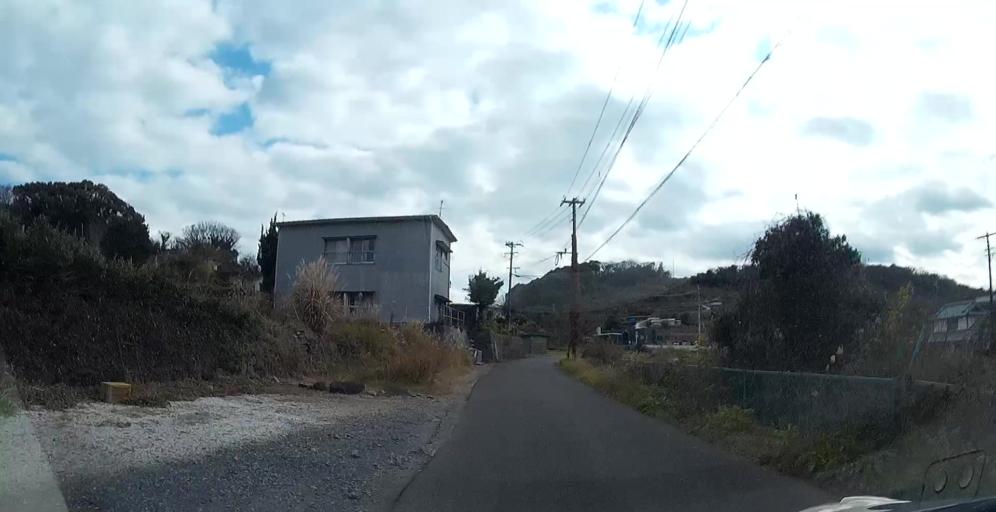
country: JP
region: Kumamoto
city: Minamata
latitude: 32.2083
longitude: 130.3867
